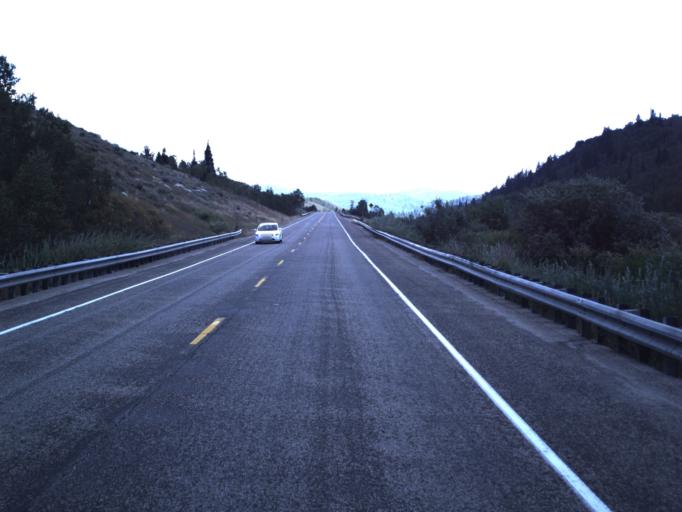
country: US
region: Utah
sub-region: Cache County
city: Richmond
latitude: 41.9111
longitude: -111.5626
